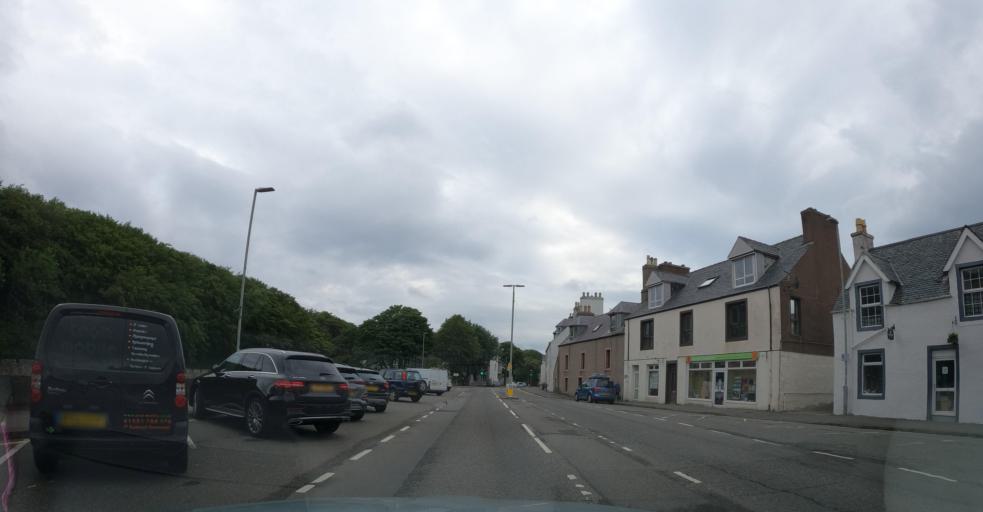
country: GB
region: Scotland
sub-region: Eilean Siar
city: Stornoway
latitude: 58.2121
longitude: -6.3880
